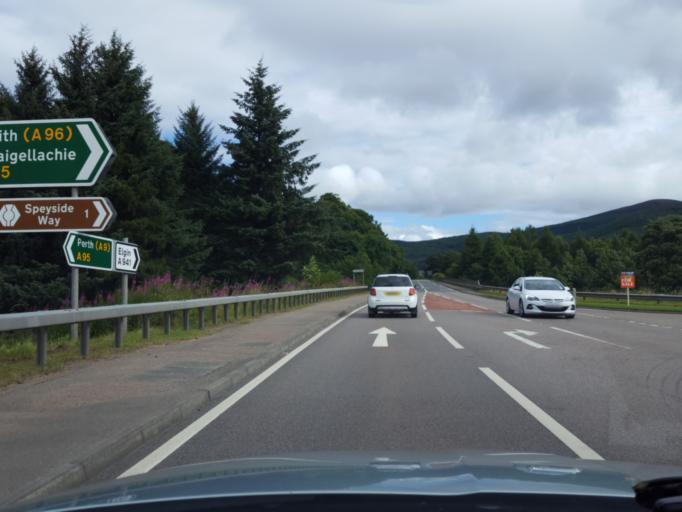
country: GB
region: Scotland
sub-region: Moray
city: Rothes
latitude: 57.4901
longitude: -3.1925
